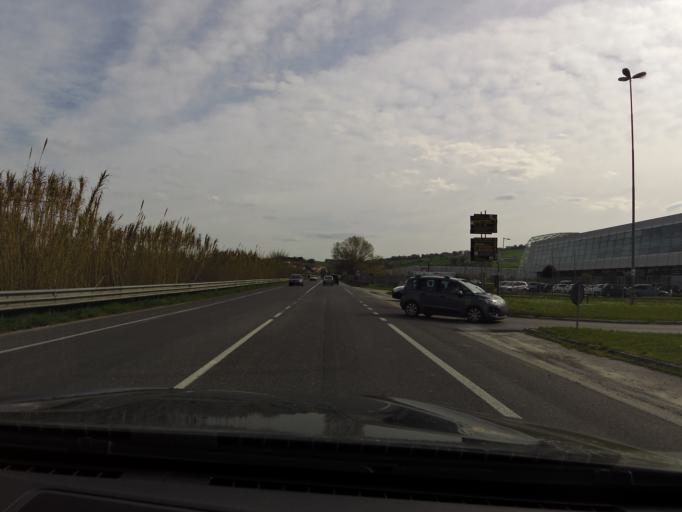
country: IT
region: The Marches
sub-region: Provincia di Ancona
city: Camerano
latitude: 43.5034
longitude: 13.5335
